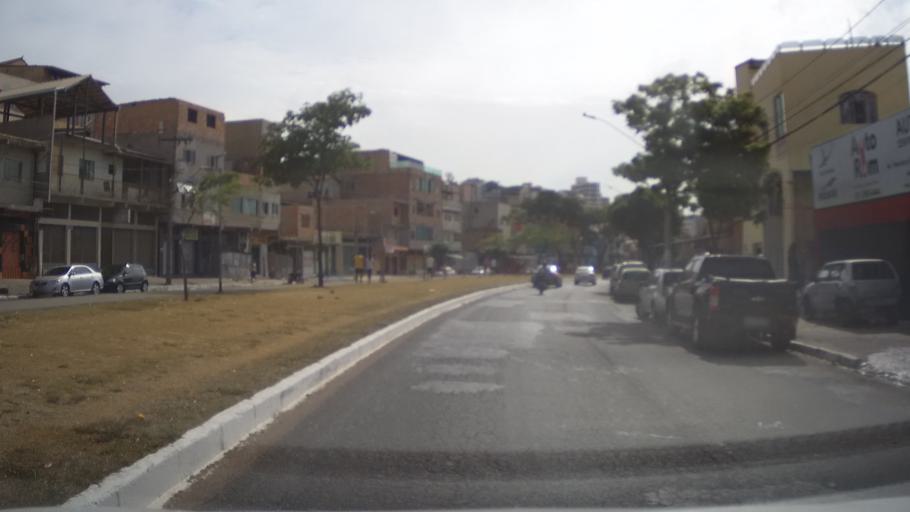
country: BR
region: Minas Gerais
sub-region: Contagem
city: Contagem
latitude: -19.9458
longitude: -44.0502
